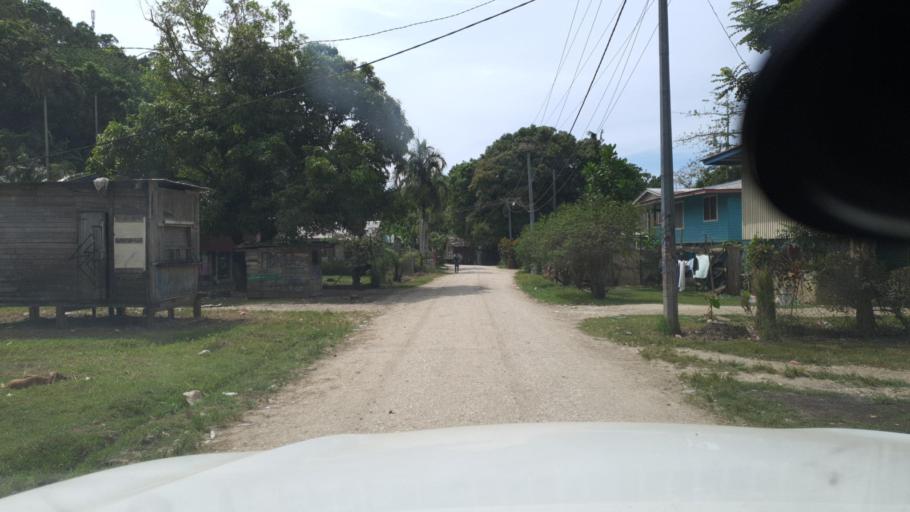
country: SB
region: Guadalcanal
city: Honiara
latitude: -9.4290
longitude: 159.9193
